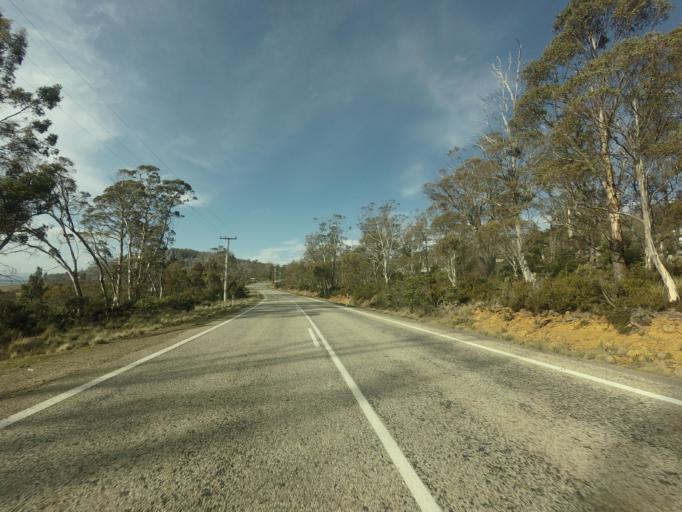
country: AU
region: Tasmania
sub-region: Meander Valley
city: Deloraine
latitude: -41.9908
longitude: 146.6887
